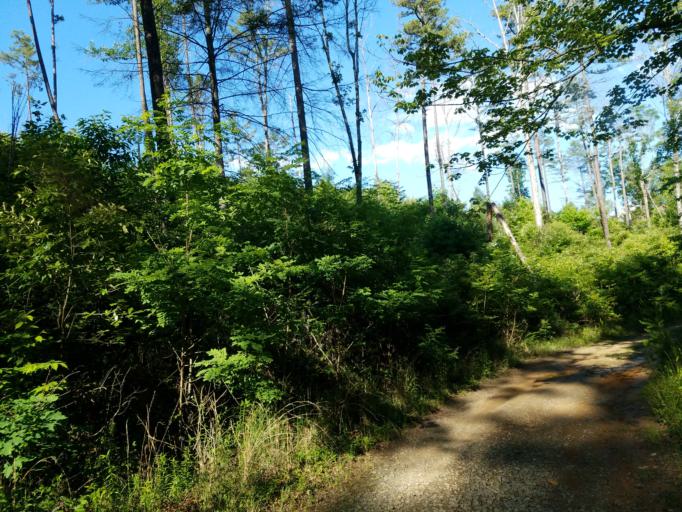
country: US
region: Georgia
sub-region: Fannin County
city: Blue Ridge
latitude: 34.7968
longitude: -84.1964
